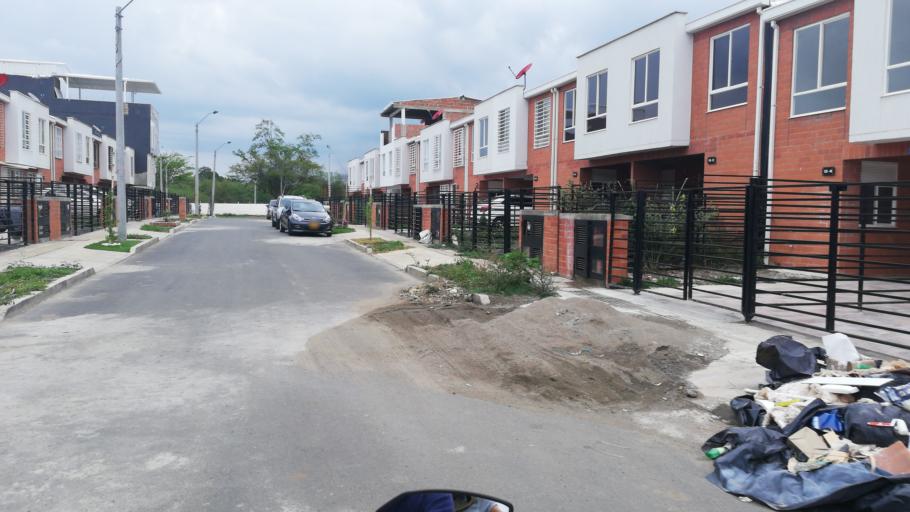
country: CO
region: Valle del Cauca
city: Jamundi
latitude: 3.3464
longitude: -76.5190
